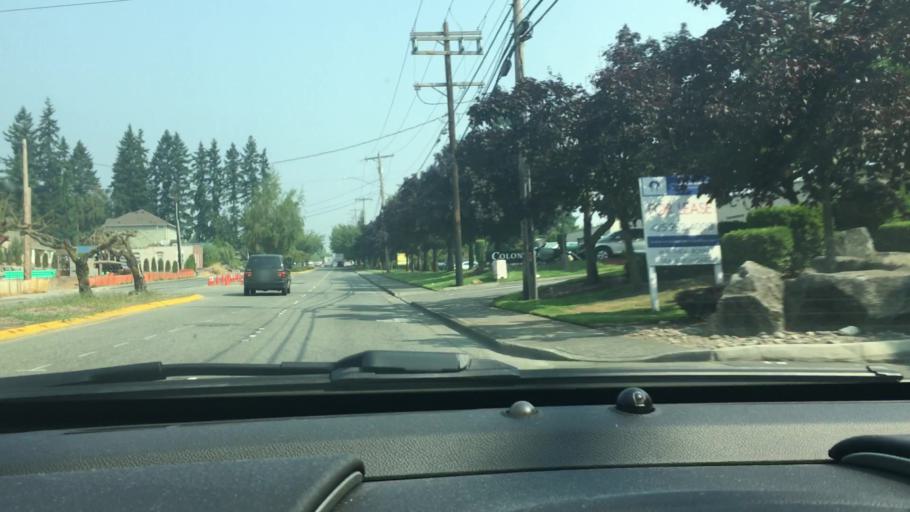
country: US
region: Washington
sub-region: Snohomish County
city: Alderwood Manor
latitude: 47.8254
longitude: -122.2817
